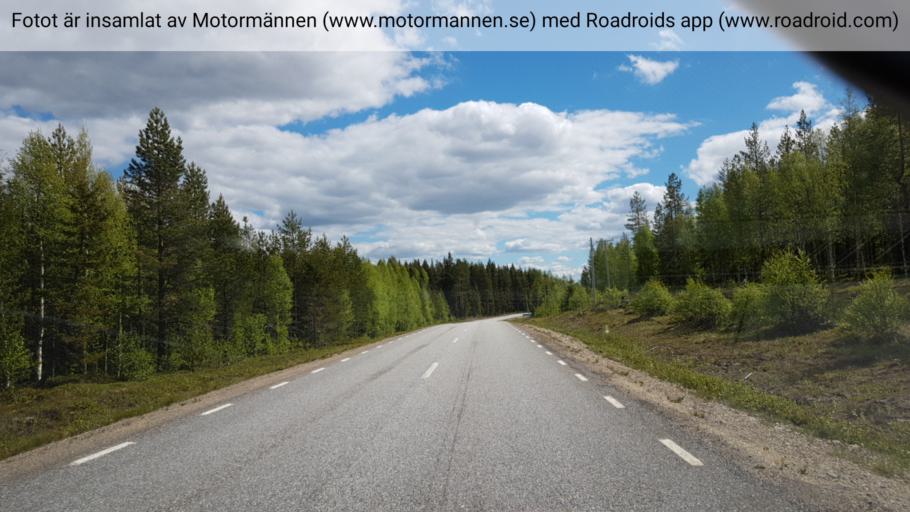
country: SE
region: Vaesterbotten
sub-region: Skelleftea Kommun
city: Langsele
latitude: 64.6908
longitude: 20.0206
